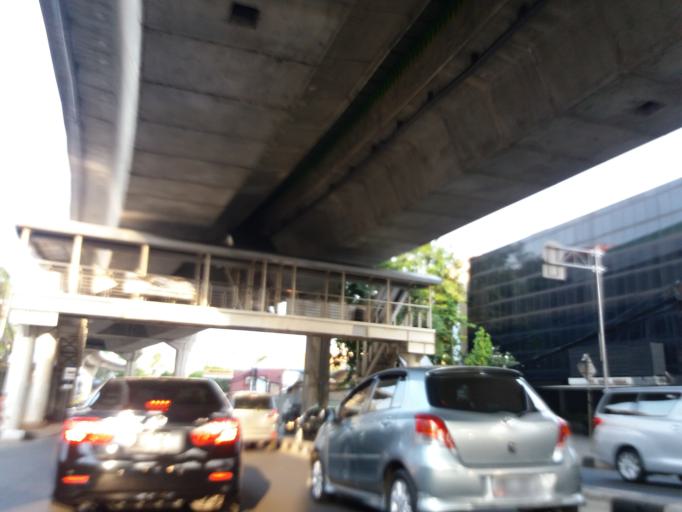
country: ID
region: Jakarta Raya
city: Jakarta
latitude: -6.2389
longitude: 106.8156
